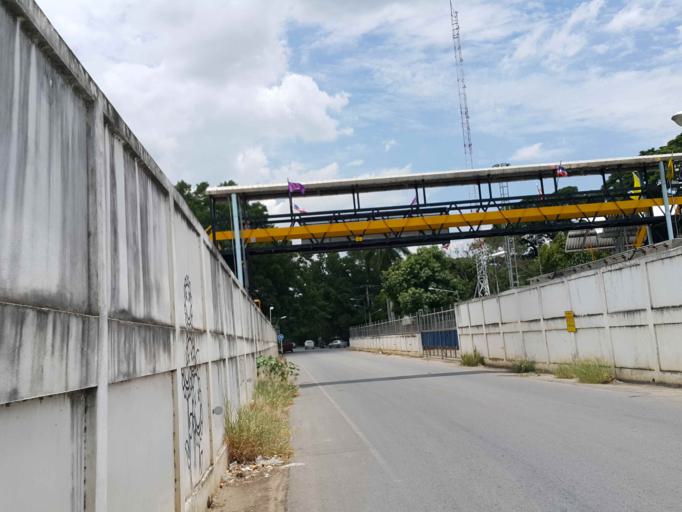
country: TH
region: Chiang Mai
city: Chiang Mai
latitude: 18.7762
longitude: 99.0174
